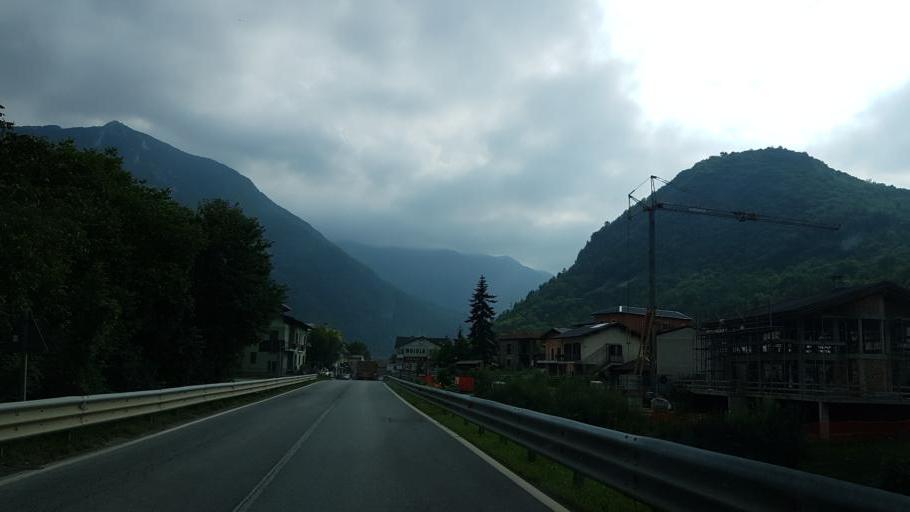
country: IT
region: Piedmont
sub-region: Provincia di Cuneo
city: Moiola
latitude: 44.3212
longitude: 7.3911
